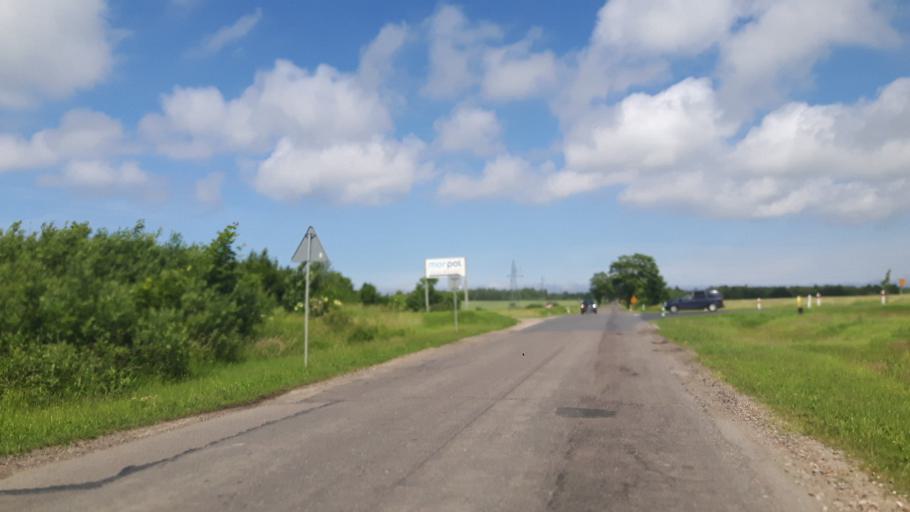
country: PL
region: Pomeranian Voivodeship
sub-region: Powiat slupski
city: Ustka
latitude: 54.5526
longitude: 16.8364
